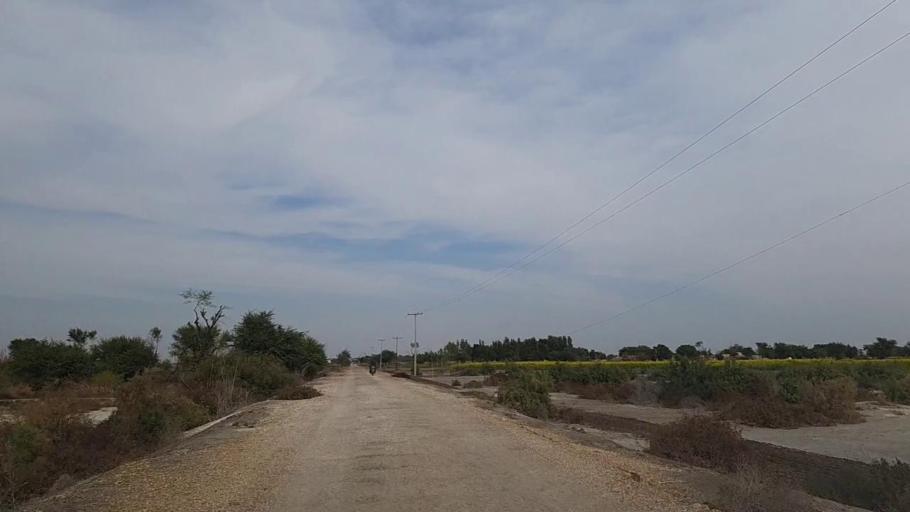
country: PK
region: Sindh
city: Jam Sahib
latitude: 26.4071
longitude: 68.5455
